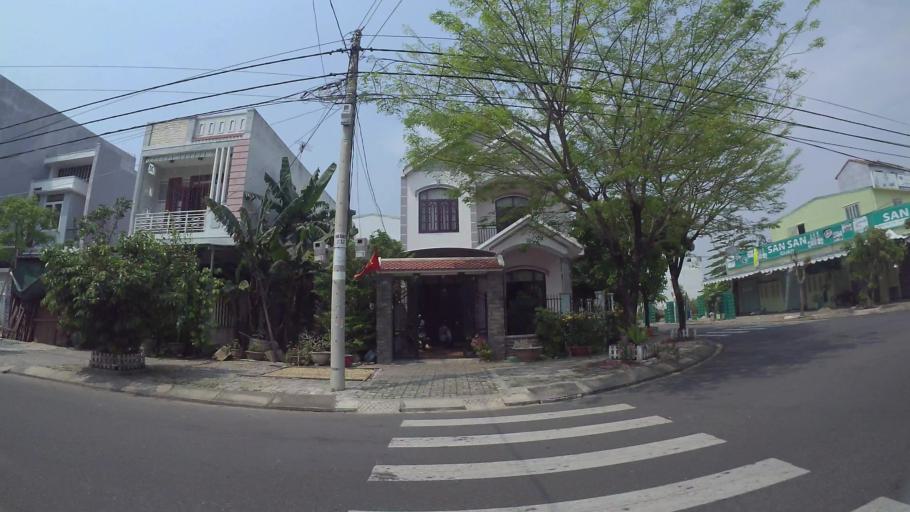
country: VN
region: Da Nang
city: Cam Le
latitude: 15.9868
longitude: 108.2138
